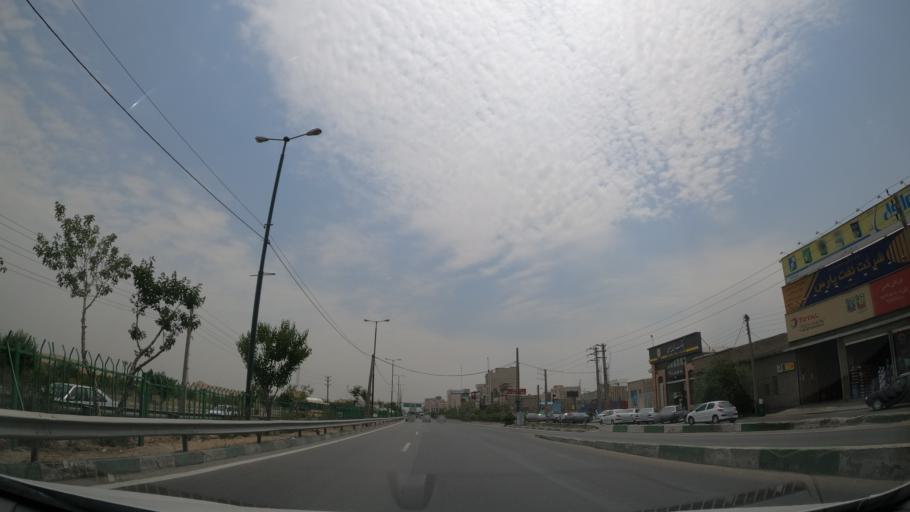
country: IR
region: Tehran
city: Eslamshahr
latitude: 35.6772
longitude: 51.2695
